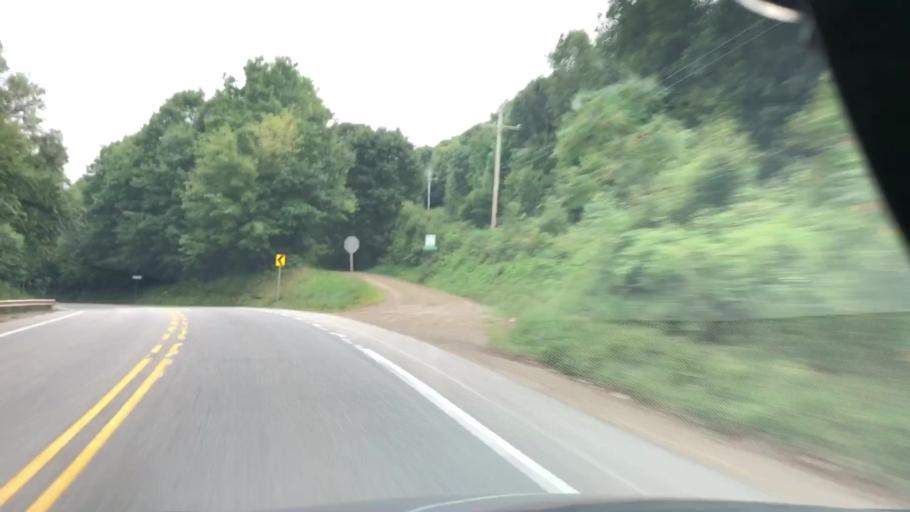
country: US
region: Pennsylvania
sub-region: Venango County
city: Hasson Heights
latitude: 41.5216
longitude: -79.7097
